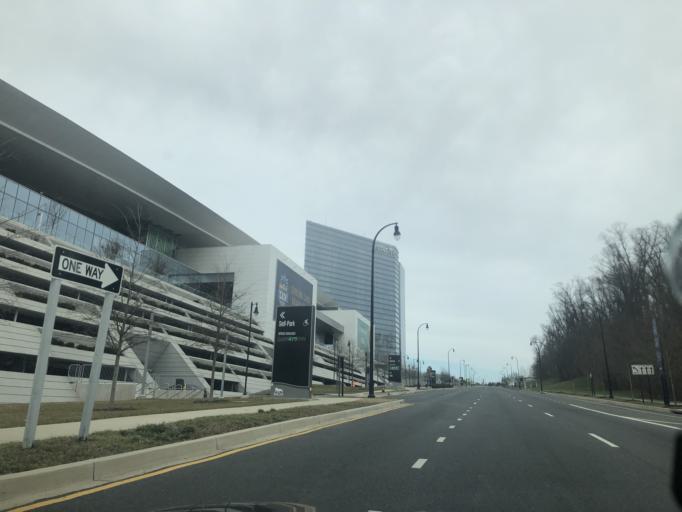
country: US
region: Maryland
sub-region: Prince George's County
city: Forest Heights
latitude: 38.7938
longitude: -77.0093
